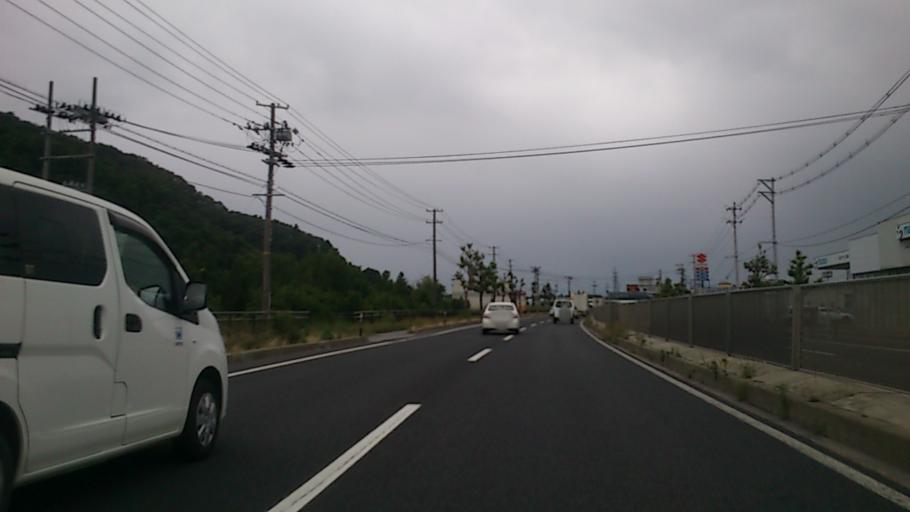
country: JP
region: Yamagata
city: Tendo
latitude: 38.3514
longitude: 140.3863
